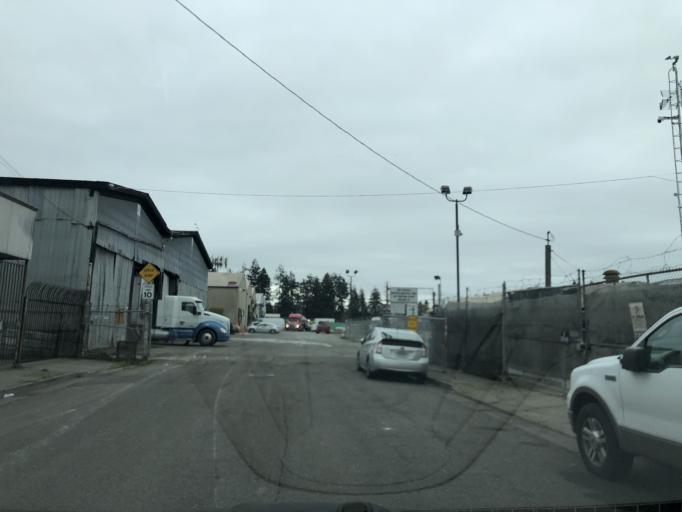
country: US
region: California
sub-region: Alameda County
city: San Leandro
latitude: 37.7397
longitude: -122.1767
